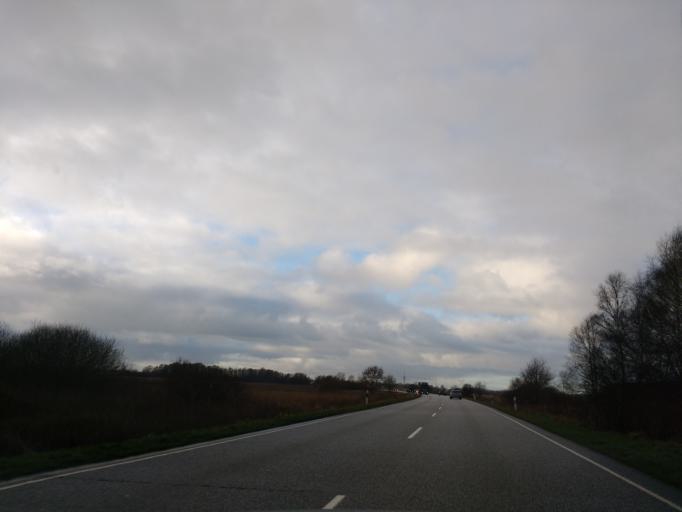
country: DE
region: Schleswig-Holstein
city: Heiligenstedten
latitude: 53.9384
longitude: 9.4630
